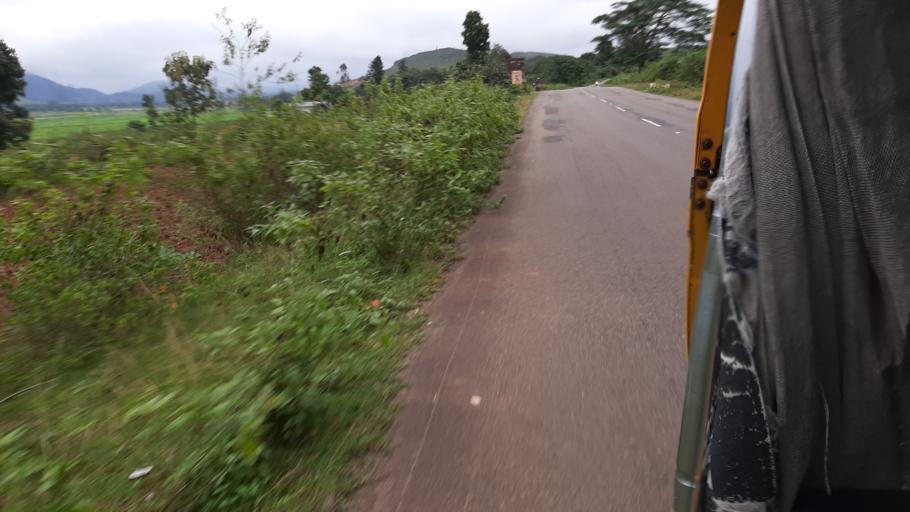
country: IN
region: Andhra Pradesh
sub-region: Vizianagaram District
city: Salur
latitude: 18.2985
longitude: 82.9125
